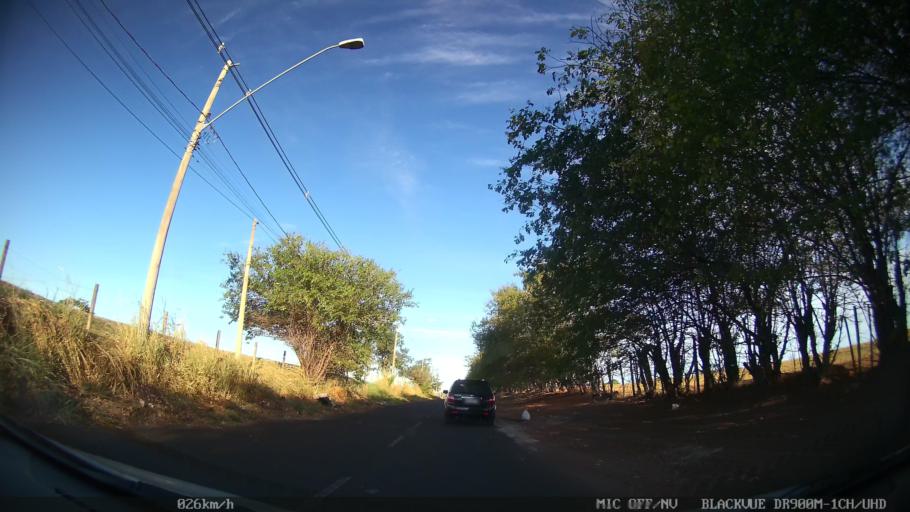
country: BR
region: Sao Paulo
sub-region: Sao Jose Do Rio Preto
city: Sao Jose do Rio Preto
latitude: -20.8665
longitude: -49.3304
